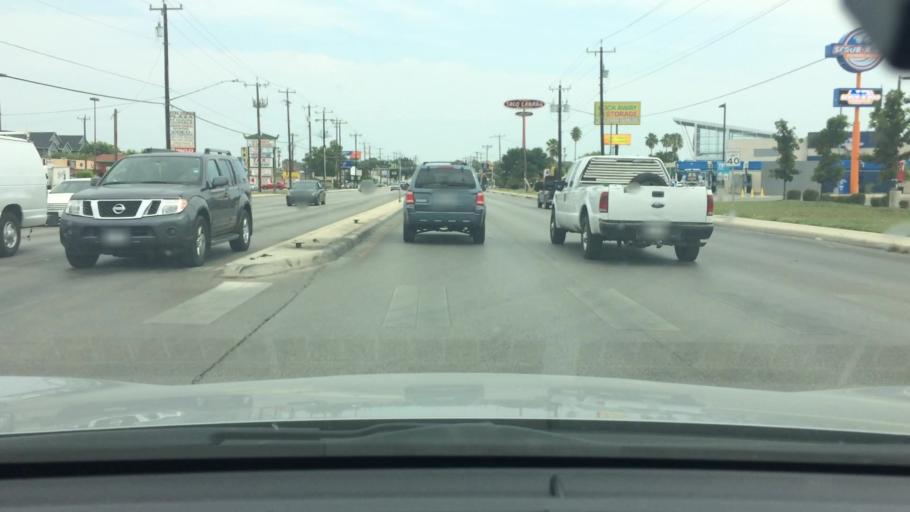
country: US
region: Texas
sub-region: Bexar County
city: Leon Valley
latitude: 29.4666
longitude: -98.6470
